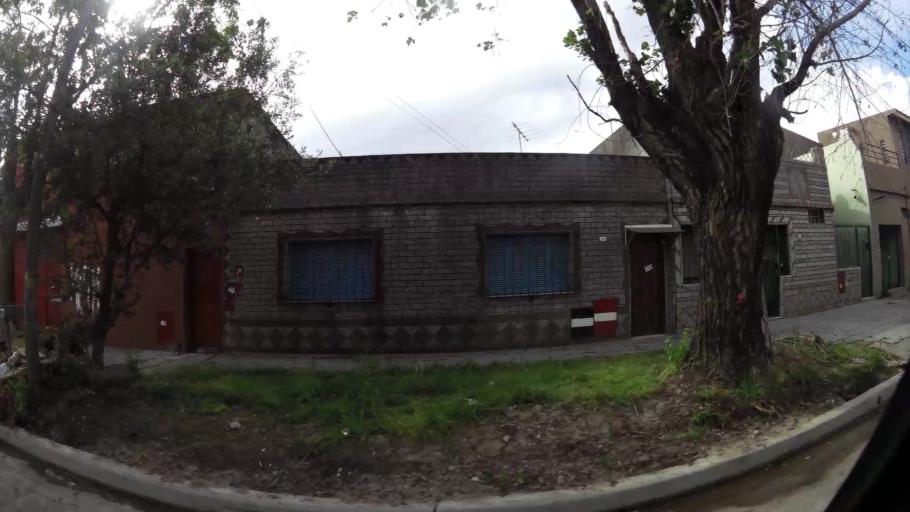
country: AR
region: Buenos Aires
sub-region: Partido de Lanus
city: Lanus
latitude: -34.6948
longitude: -58.3760
